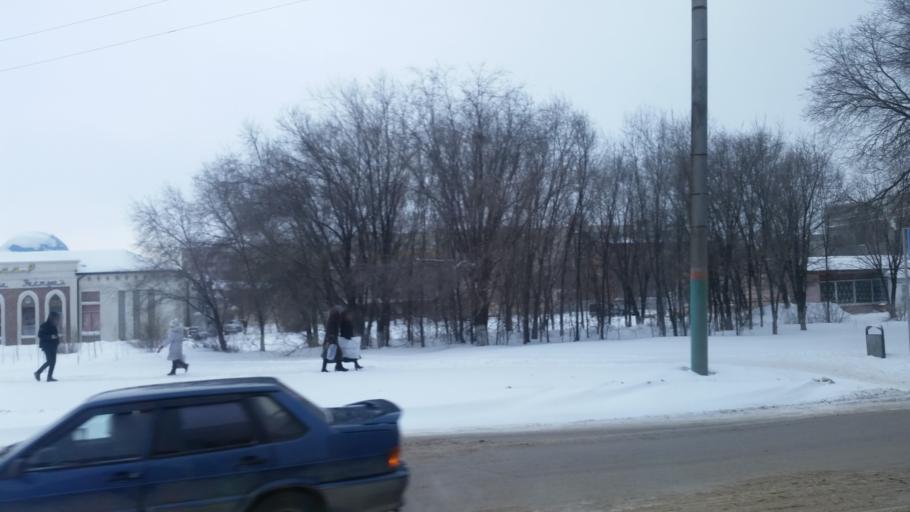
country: KZ
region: Qaraghandy
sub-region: Qaraghandy Qalasy
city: Karagandy
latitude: 49.7717
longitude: 73.1442
